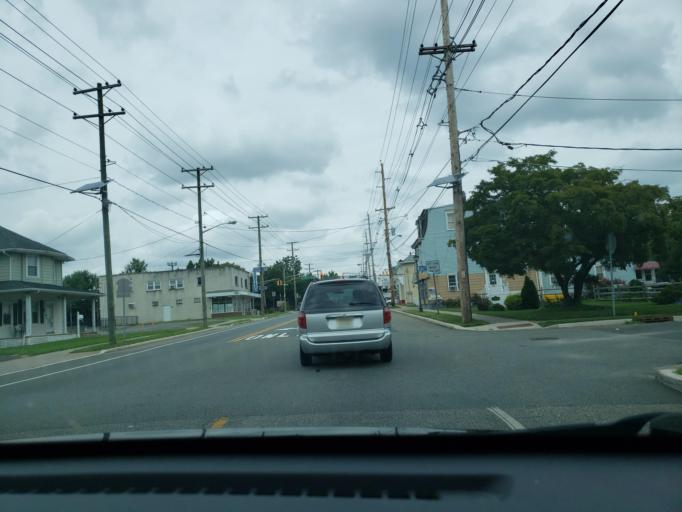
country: US
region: New Jersey
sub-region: Camden County
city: Glendora
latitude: 39.8374
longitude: -75.0683
